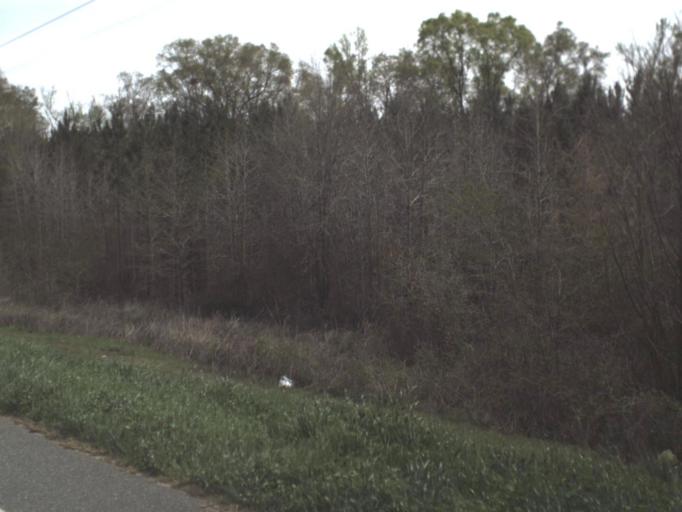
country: US
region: Alabama
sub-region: Houston County
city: Cottonwood
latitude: 30.9388
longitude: -85.3310
